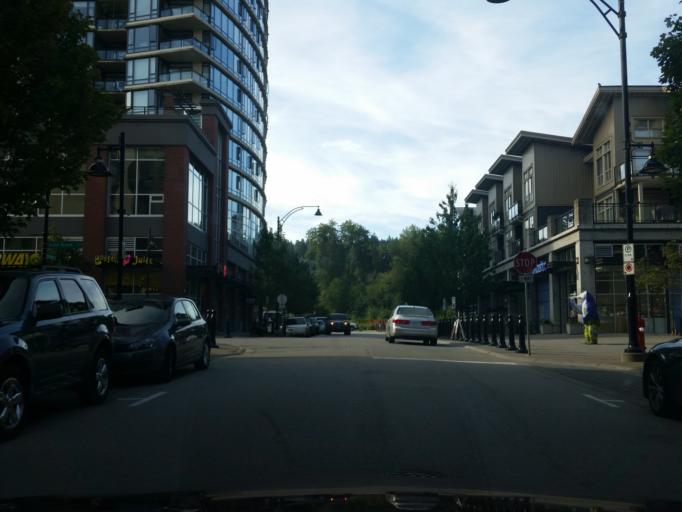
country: CA
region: British Columbia
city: Port Moody
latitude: 49.2796
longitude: -122.8291
